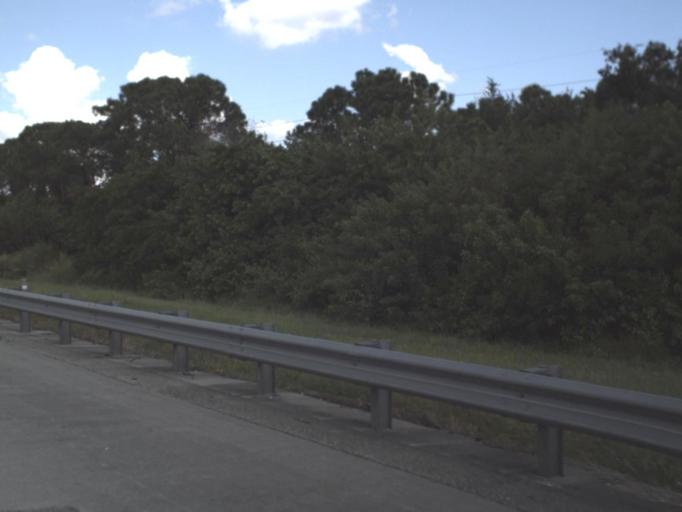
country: US
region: Florida
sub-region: Martin County
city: Palm City
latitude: 27.1342
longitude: -80.2861
